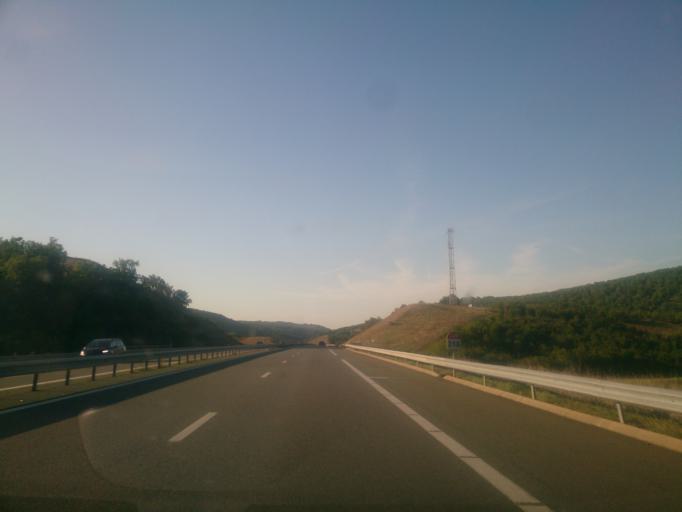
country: FR
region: Midi-Pyrenees
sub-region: Departement du Lot
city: Le Vigan
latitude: 44.8062
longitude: 1.5053
